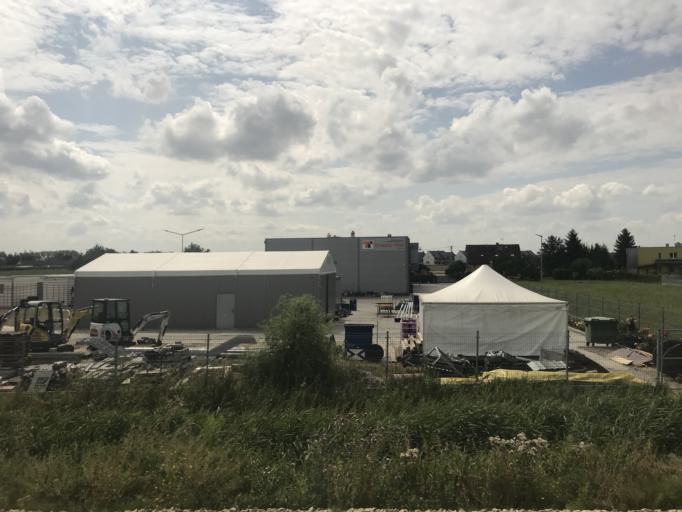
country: PL
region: Greater Poland Voivodeship
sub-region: Powiat poznanski
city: Pobiedziska
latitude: 52.4769
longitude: 17.2637
